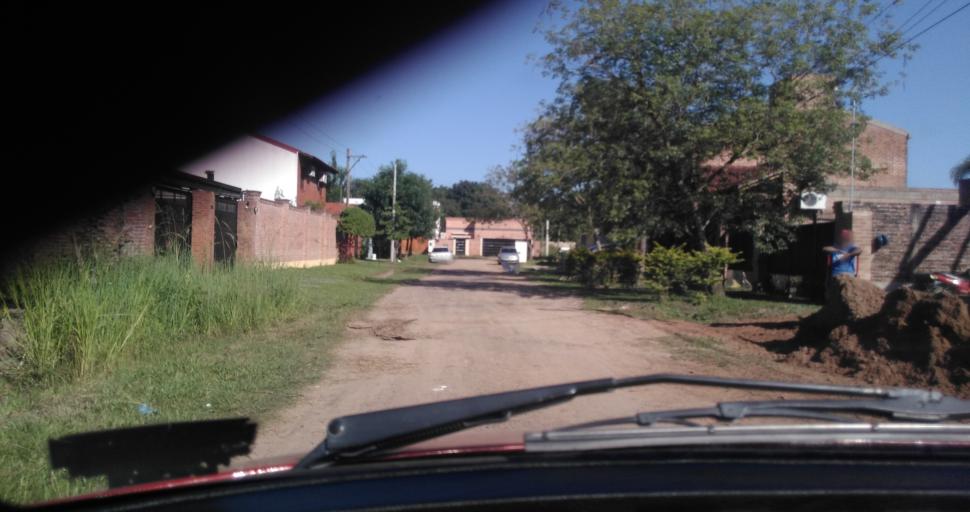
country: AR
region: Chaco
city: Resistencia
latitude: -27.4377
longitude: -58.9651
